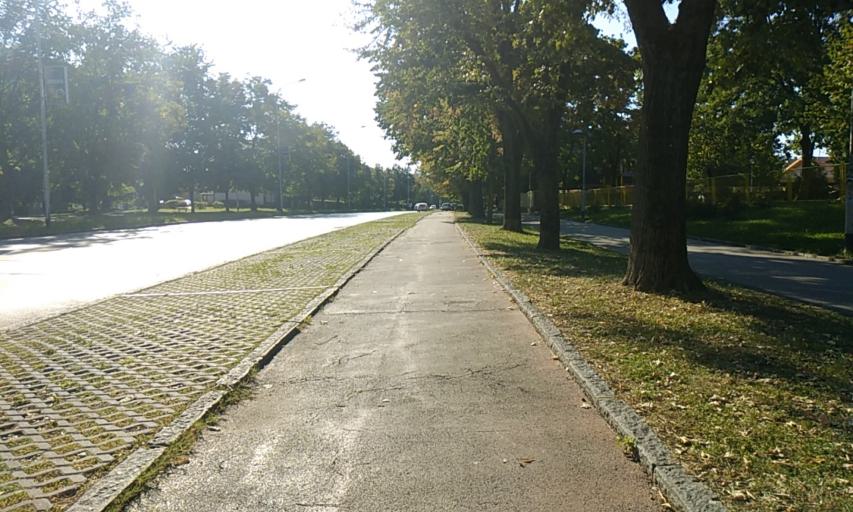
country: BA
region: Republika Srpska
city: Mejdan - Obilicevo
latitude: 44.7709
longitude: 17.2023
